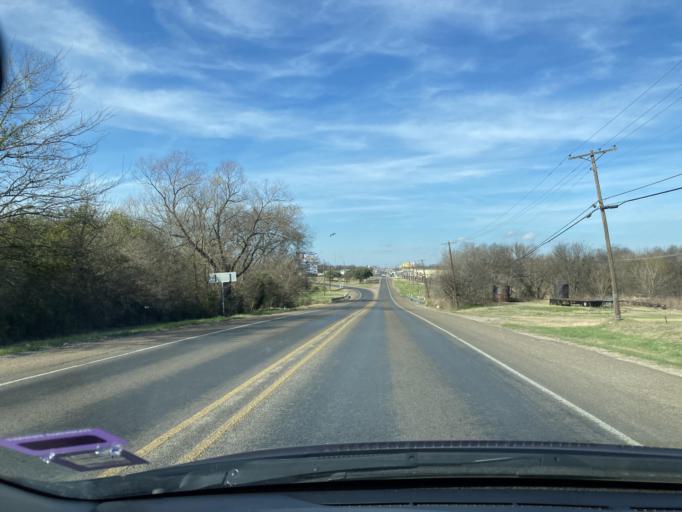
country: US
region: Texas
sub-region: Navarro County
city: Corsicana
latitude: 32.0816
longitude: -96.4507
